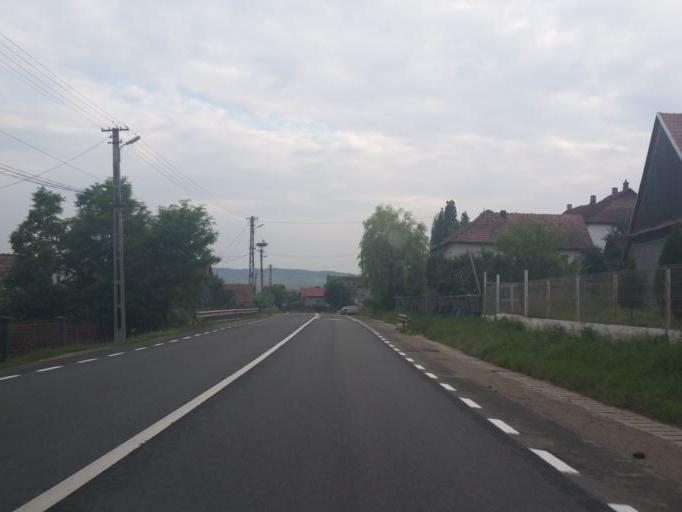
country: RO
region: Cluj
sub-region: Comuna Sanpaul
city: Sanpaul
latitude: 46.9023
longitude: 23.4168
